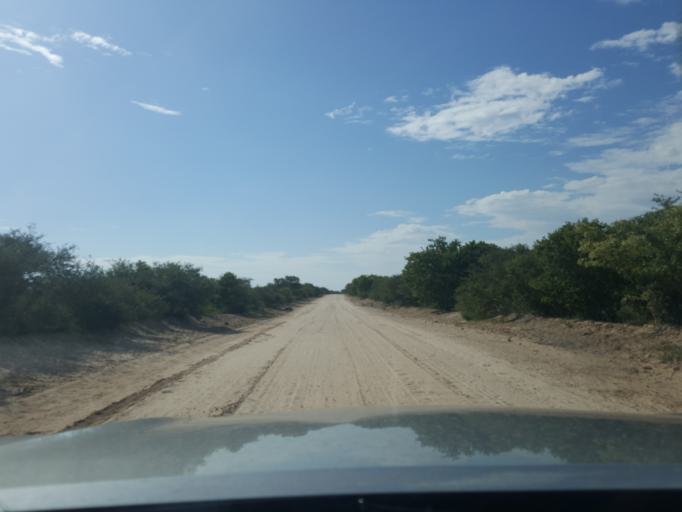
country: BW
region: Kweneng
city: Khudumelapye
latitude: -23.4903
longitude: 24.6988
